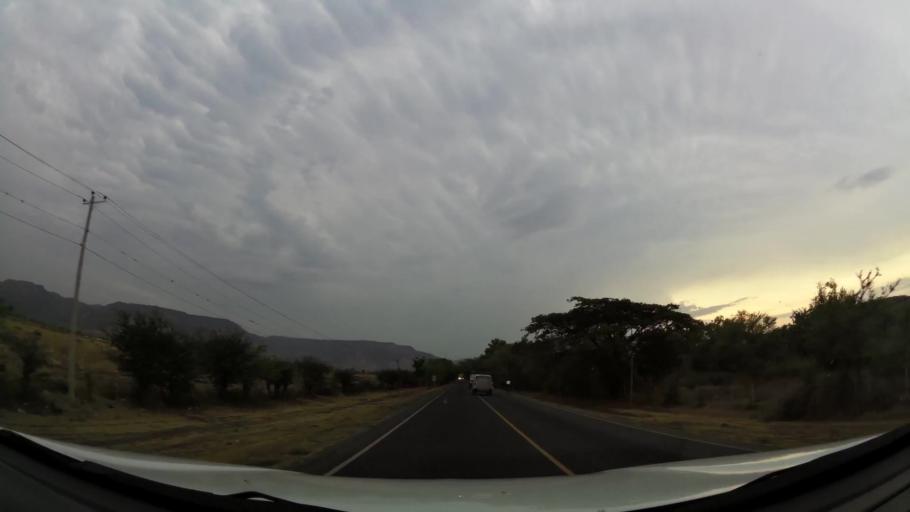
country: NI
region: Matagalpa
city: Ciudad Dario
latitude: 12.9085
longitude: -86.1745
